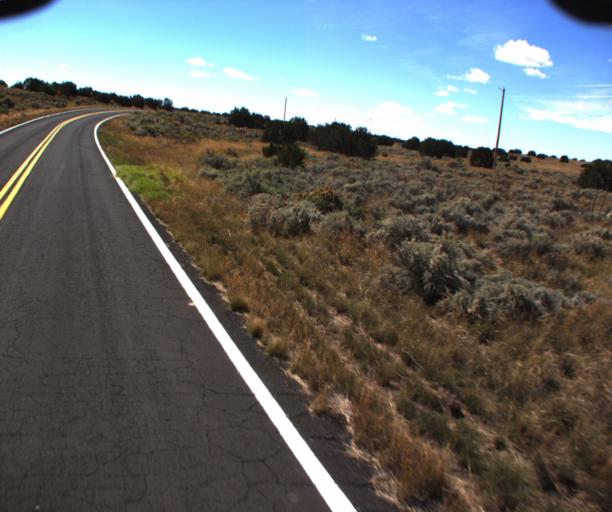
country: US
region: Arizona
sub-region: Apache County
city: Houck
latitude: 34.9286
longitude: -109.1994
